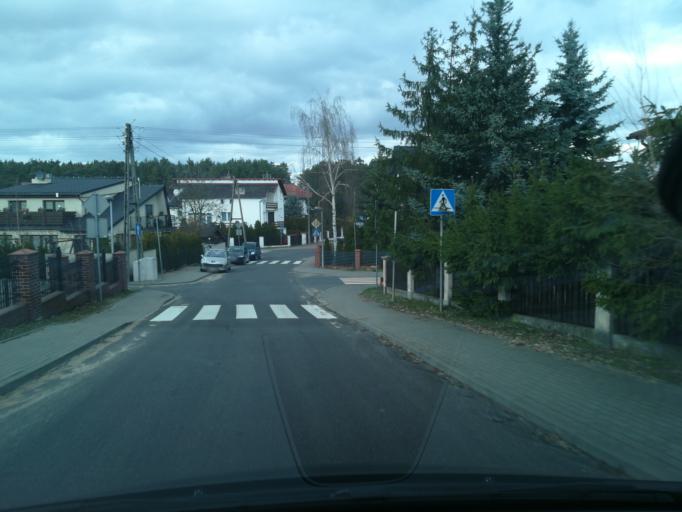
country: PL
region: Kujawsko-Pomorskie
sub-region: Powiat torunski
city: Lubicz Dolny
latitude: 52.9770
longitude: 18.6861
